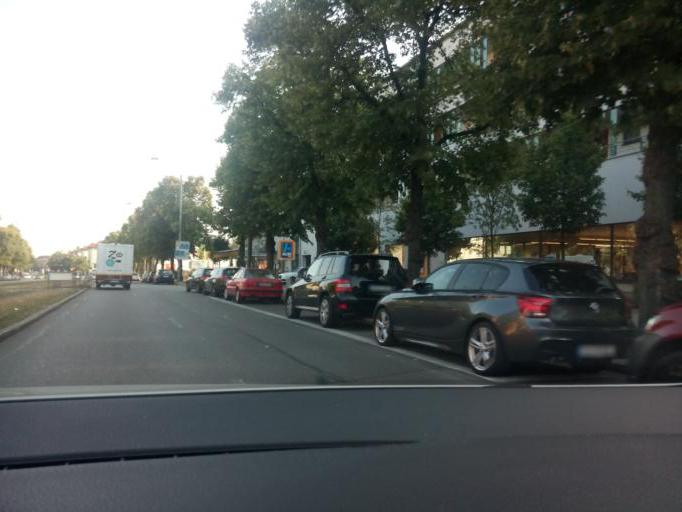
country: DE
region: Bavaria
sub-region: Upper Bavaria
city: Munich
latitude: 48.1039
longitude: 11.5972
